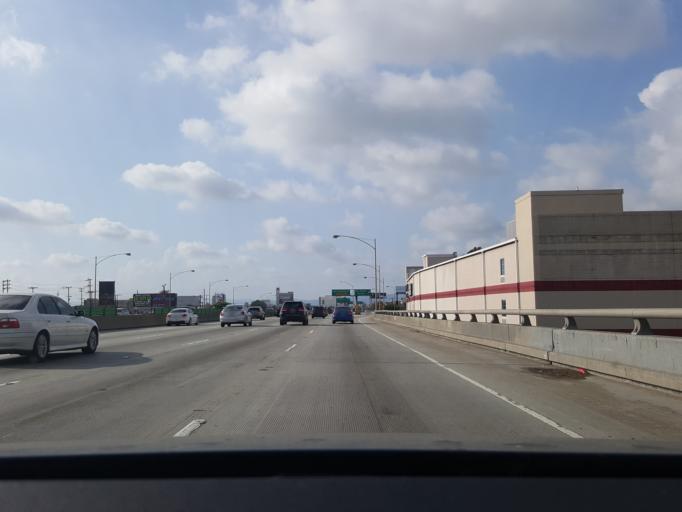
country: US
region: California
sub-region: Los Angeles County
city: Los Angeles
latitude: 34.0260
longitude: -118.2490
